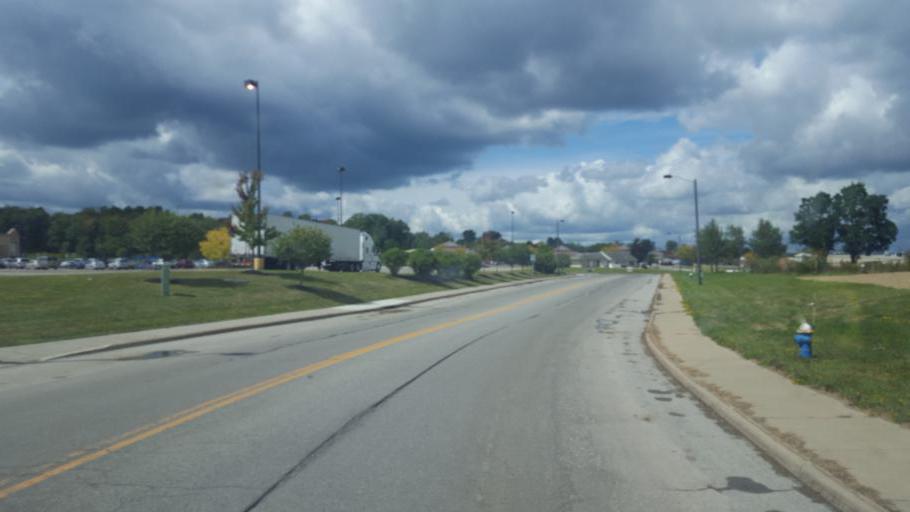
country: US
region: Ohio
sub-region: Geauga County
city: Middlefield
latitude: 41.4597
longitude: -81.0832
